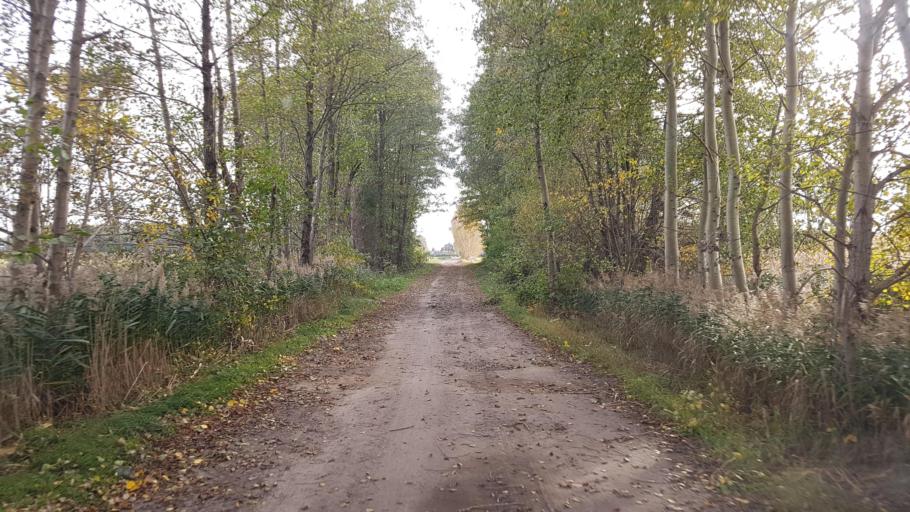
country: DE
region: Brandenburg
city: Schraden
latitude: 51.4471
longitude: 13.6922
